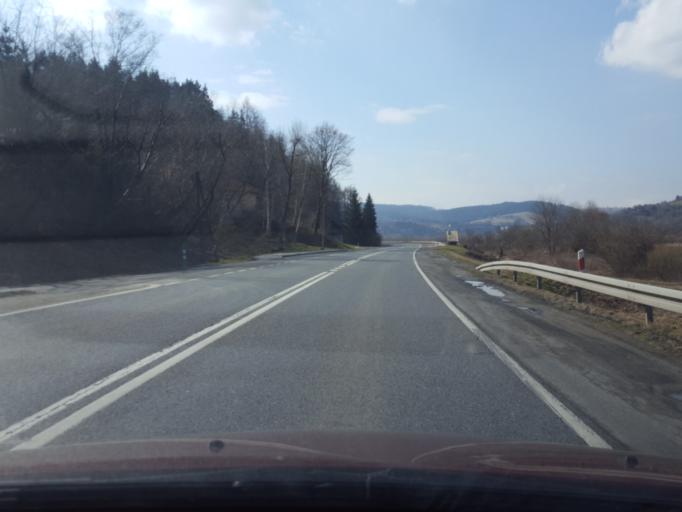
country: PL
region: Lesser Poland Voivodeship
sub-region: Powiat nowosadecki
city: Chelmiec
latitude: 49.6832
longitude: 20.6550
